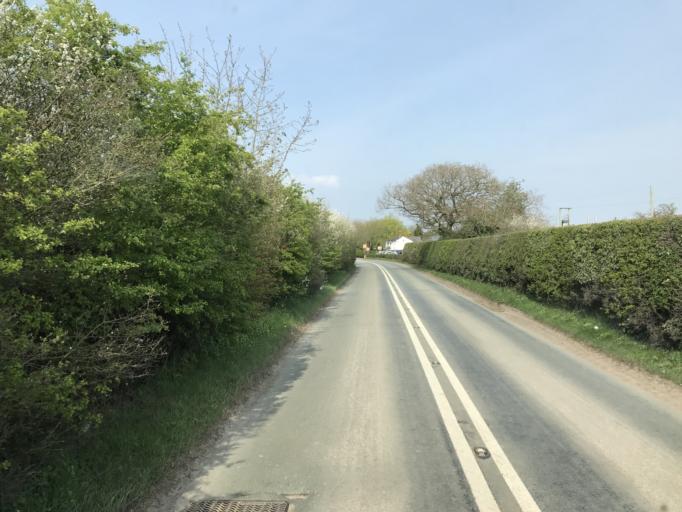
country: GB
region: England
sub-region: Cheshire West and Chester
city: Eccleston
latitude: 53.1688
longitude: -2.8612
